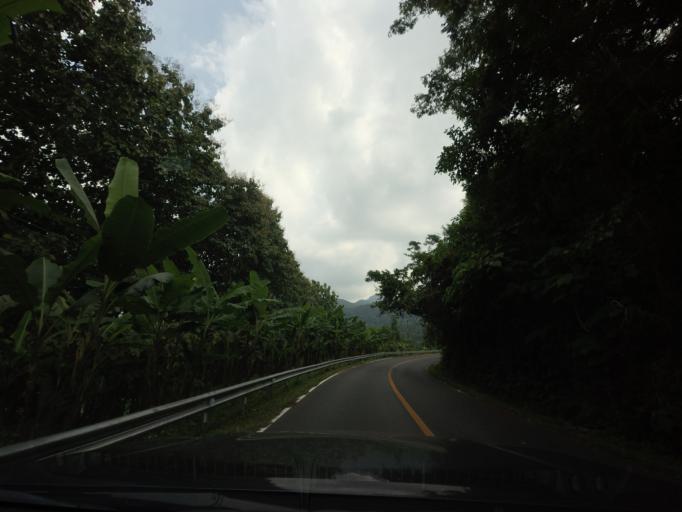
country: TH
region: Nan
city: Pua
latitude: 19.1792
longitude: 100.9630
